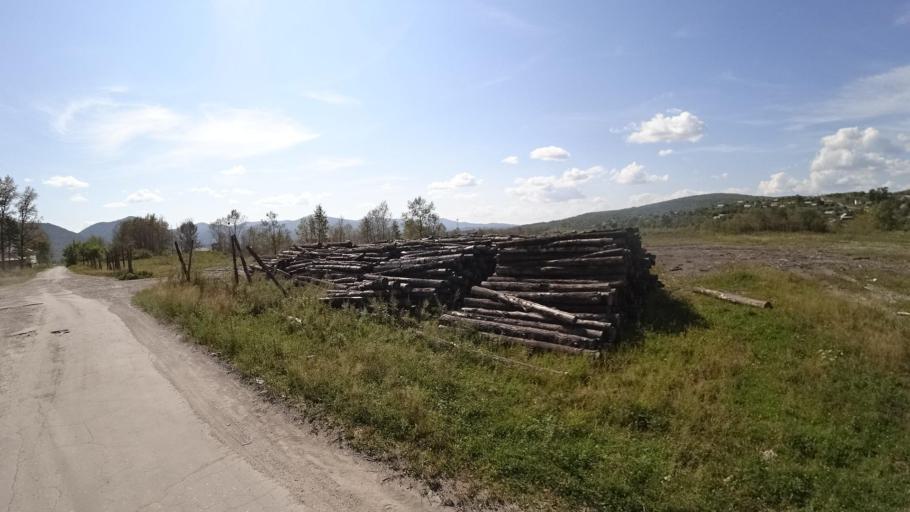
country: RU
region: Jewish Autonomous Oblast
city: Londoko
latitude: 49.0047
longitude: 131.8795
